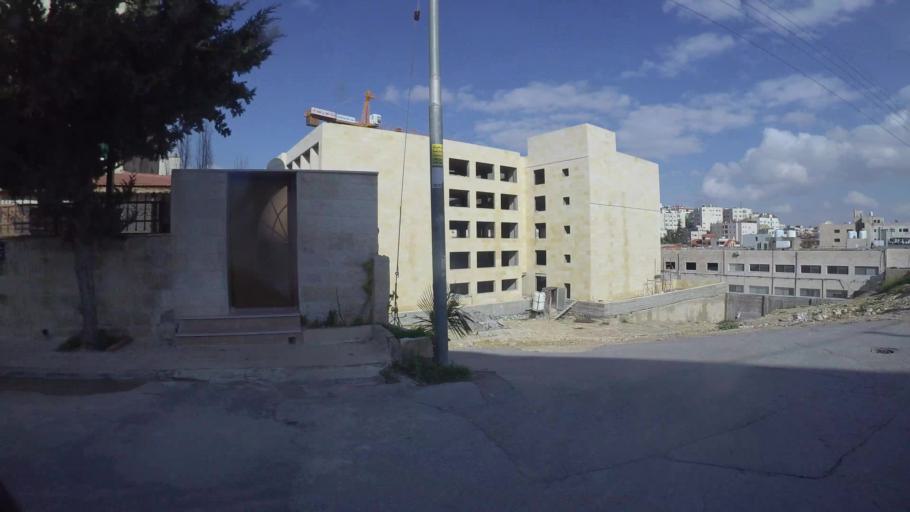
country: JO
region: Amman
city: Al Jubayhah
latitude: 32.0219
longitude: 35.8595
